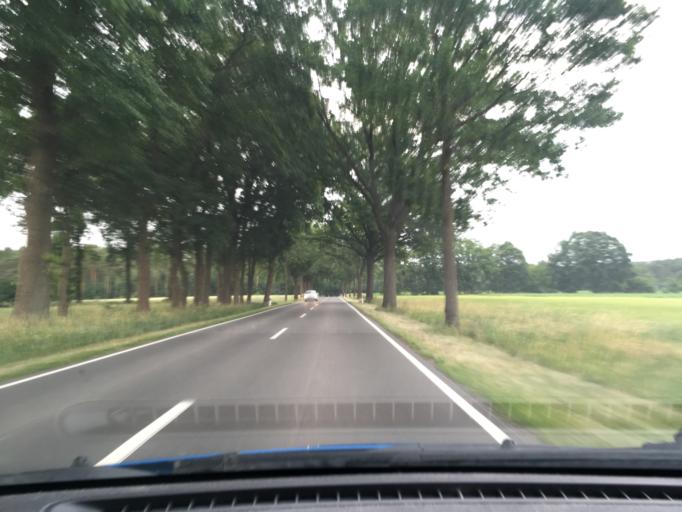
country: DE
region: Lower Saxony
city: Bad Fallingbostel
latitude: 52.8431
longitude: 9.6489
